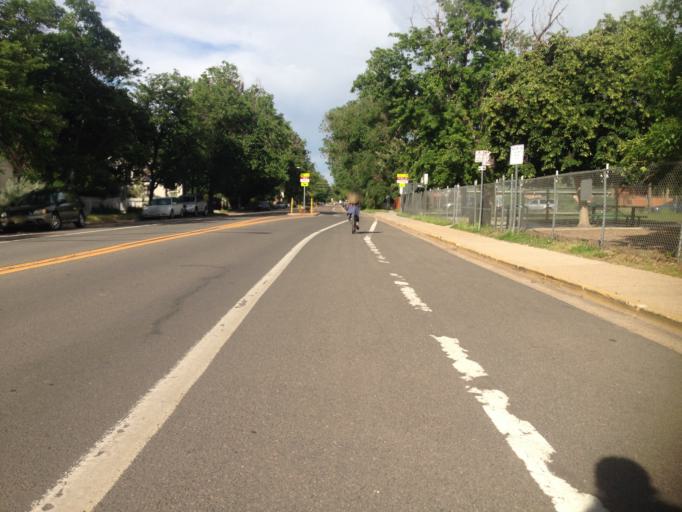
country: US
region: Colorado
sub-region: Boulder County
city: Boulder
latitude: 40.0221
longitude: -105.2697
